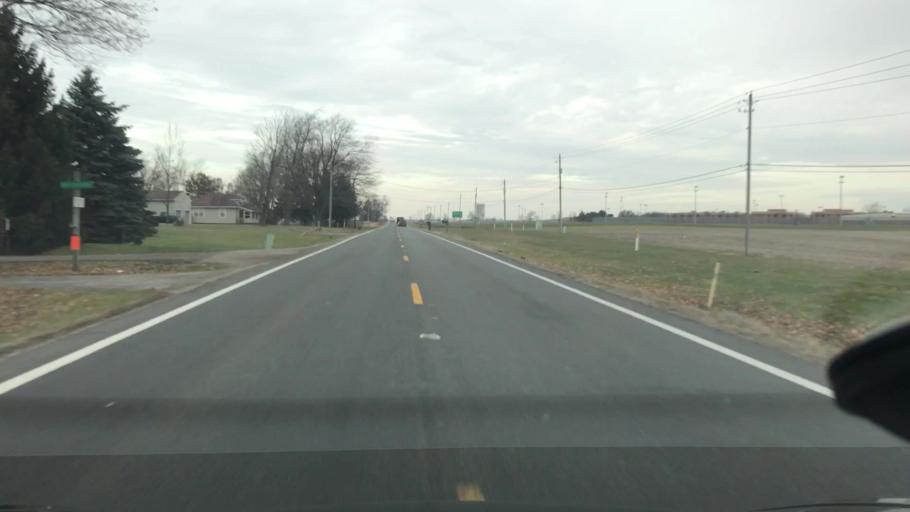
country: US
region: Ohio
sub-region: Madison County
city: London
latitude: 39.9031
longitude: -83.4679
